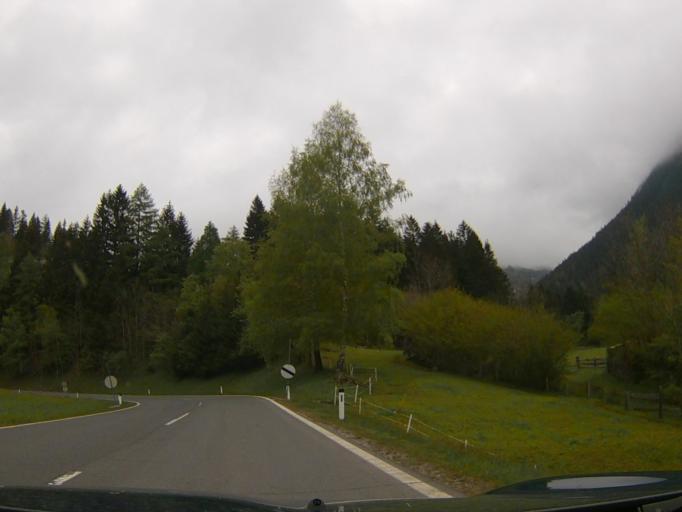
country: AT
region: Carinthia
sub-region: Politischer Bezirk Spittal an der Drau
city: Obervellach
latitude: 46.9650
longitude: 13.1850
